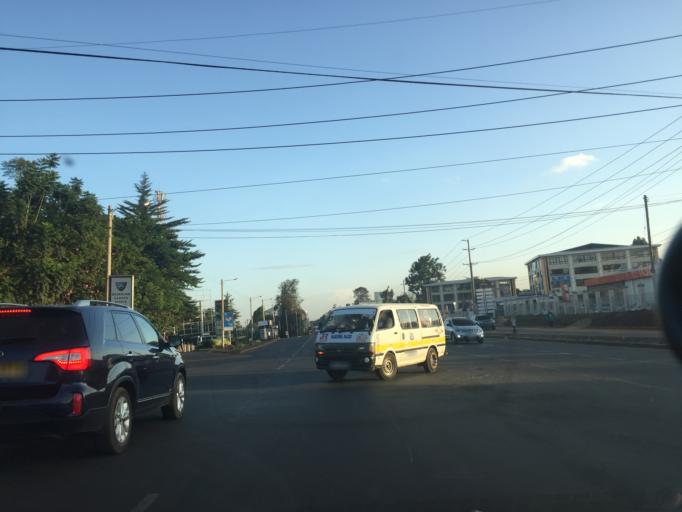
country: KE
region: Kiambu
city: Kiambu
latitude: -1.2247
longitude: 36.8386
